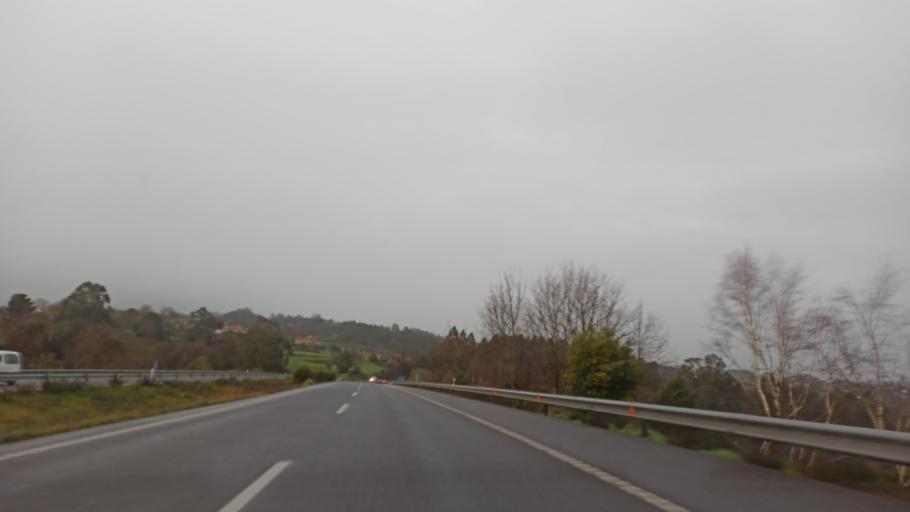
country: ES
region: Galicia
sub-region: Provincia da Coruna
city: Cambre
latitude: 43.2625
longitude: -8.3407
